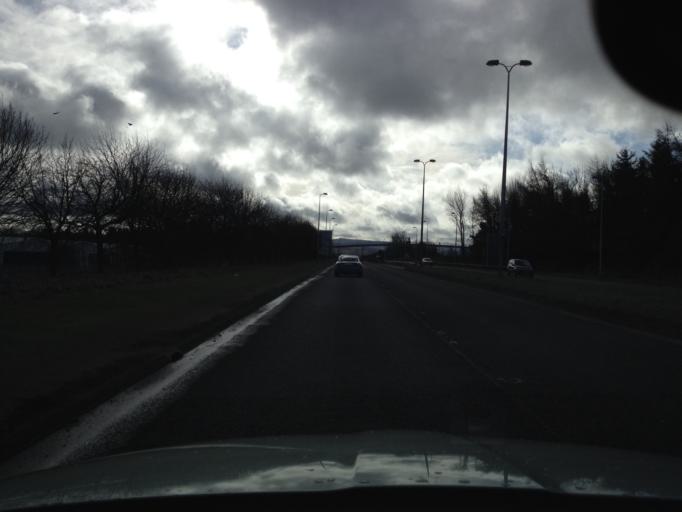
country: GB
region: Scotland
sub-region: West Lothian
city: Livingston
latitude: 55.9040
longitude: -3.5138
